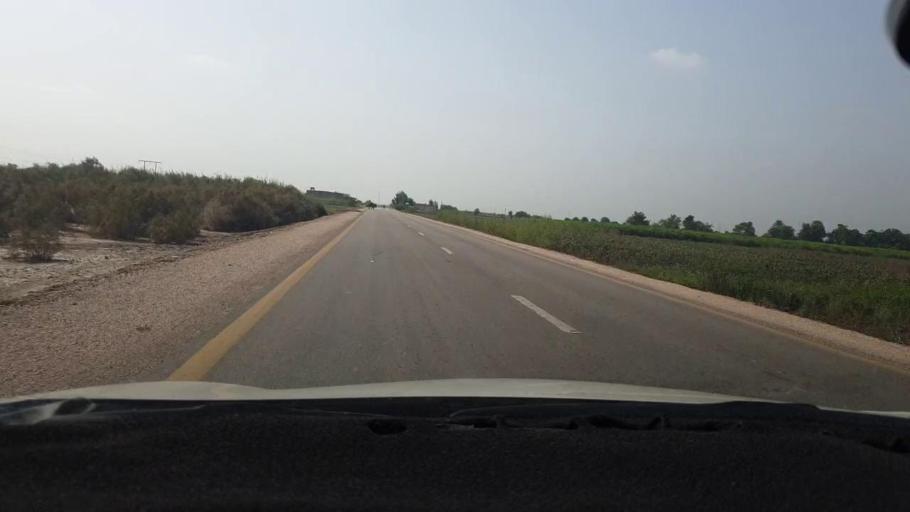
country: PK
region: Sindh
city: Jhol
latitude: 25.8517
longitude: 69.0605
